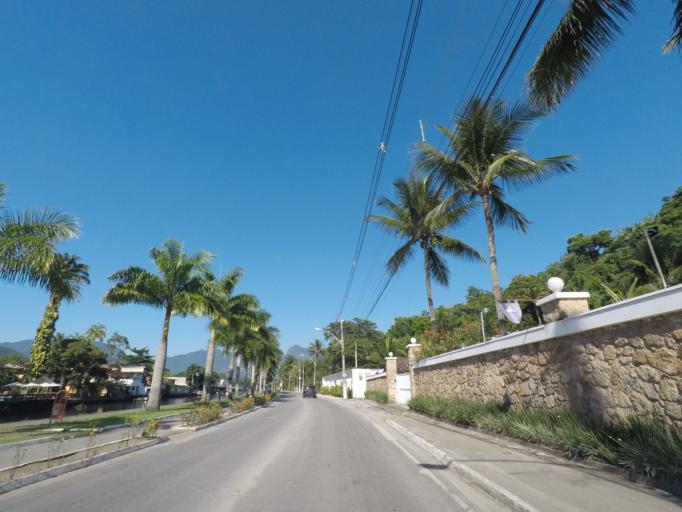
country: BR
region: Rio de Janeiro
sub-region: Parati
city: Paraty
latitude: -23.2171
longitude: -44.7176
